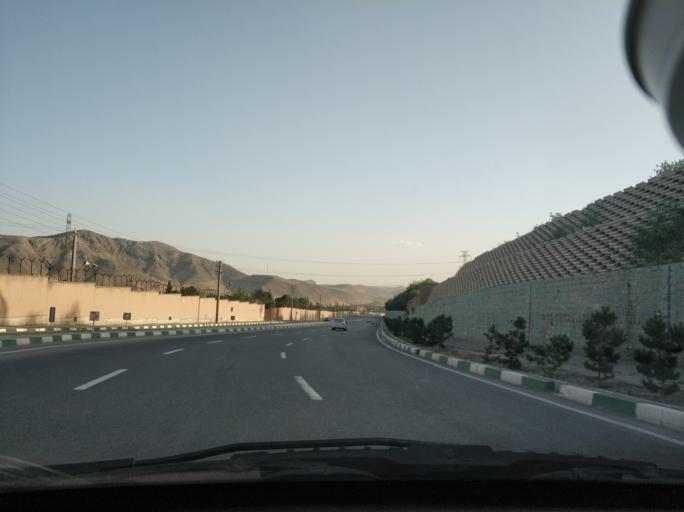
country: IR
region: Tehran
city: Tehran
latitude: 35.7407
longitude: 51.6048
